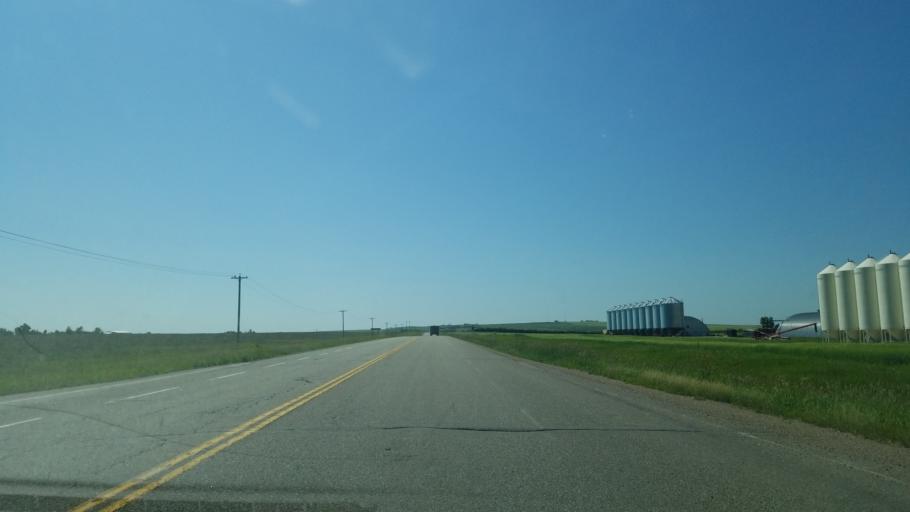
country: CA
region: Alberta
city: Provost
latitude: 52.3613
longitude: -110.1015
